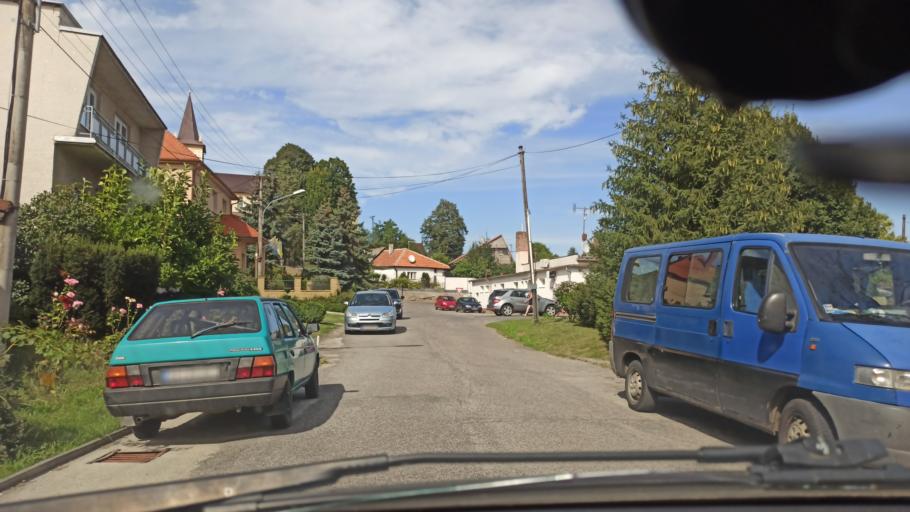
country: SK
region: Trnavsky
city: Gbely
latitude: 48.6804
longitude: 17.1993
